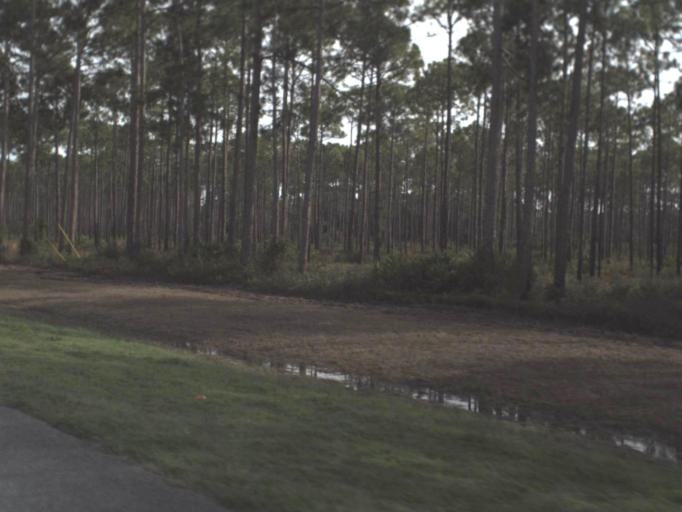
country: US
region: Florida
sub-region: Bay County
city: Mexico Beach
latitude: 29.9803
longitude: -85.4737
